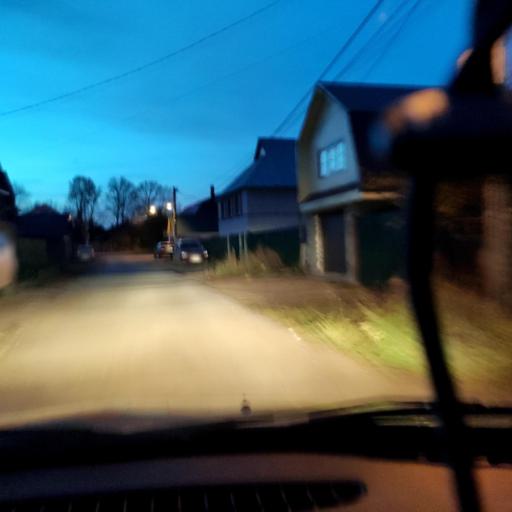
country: RU
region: Bashkortostan
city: Ufa
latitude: 54.7247
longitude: 55.9034
